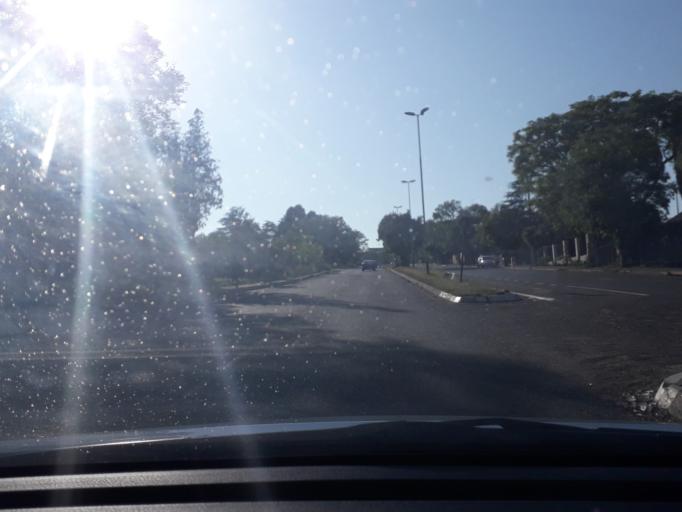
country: ZA
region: Gauteng
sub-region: City of Johannesburg Metropolitan Municipality
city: Roodepoort
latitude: -26.0920
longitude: 27.9776
